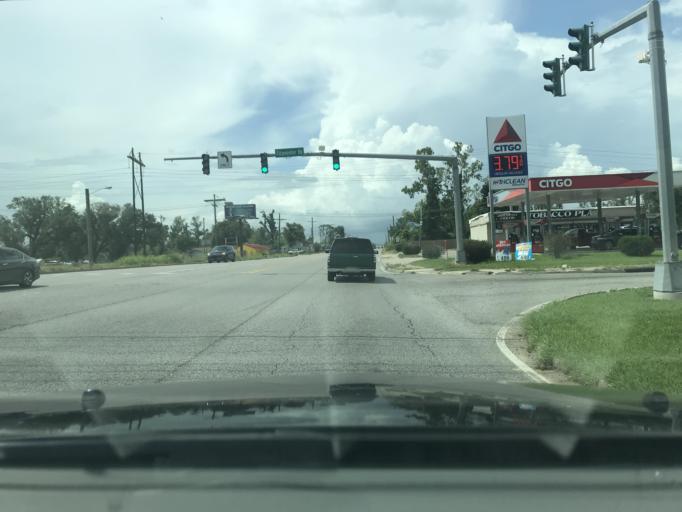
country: US
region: Louisiana
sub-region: Calcasieu Parish
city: Moss Bluff
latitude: 30.2644
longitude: -93.1807
